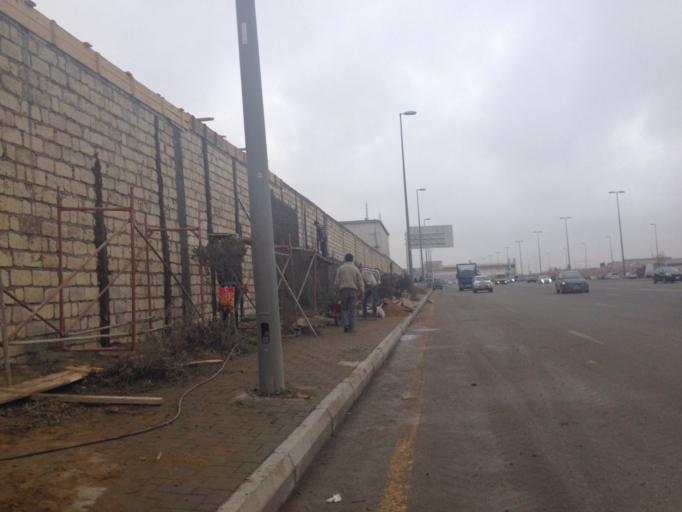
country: AZ
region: Baki
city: Baku
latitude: 40.4224
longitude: 49.8718
